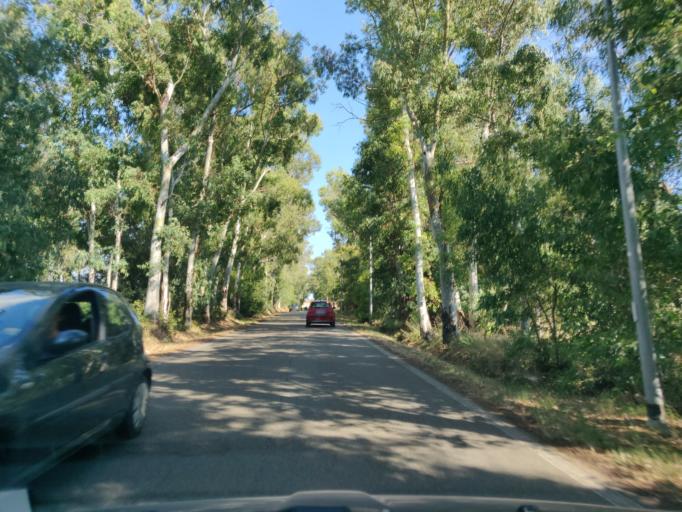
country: IT
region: Latium
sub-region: Citta metropolitana di Roma Capitale
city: Aurelia
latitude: 42.1574
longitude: 11.7522
